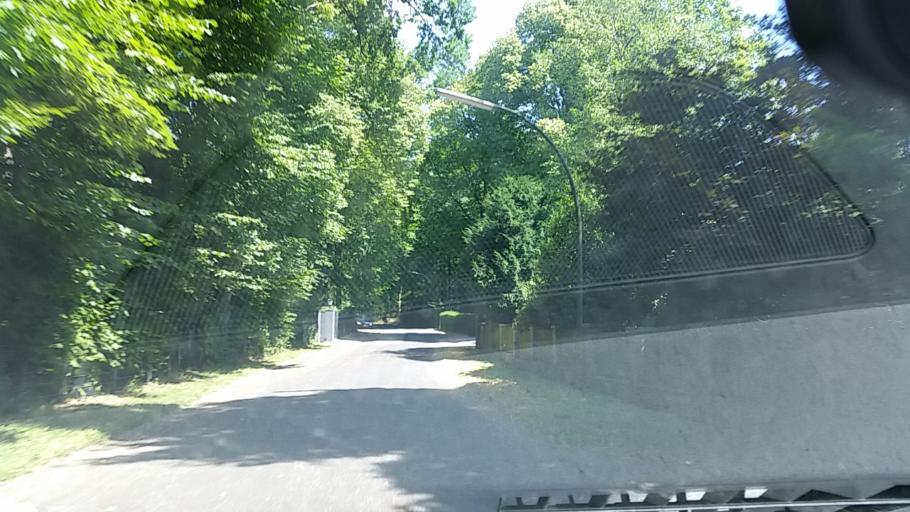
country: DE
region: Schleswig-Holstein
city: Wedel
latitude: 53.5669
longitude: 9.7712
